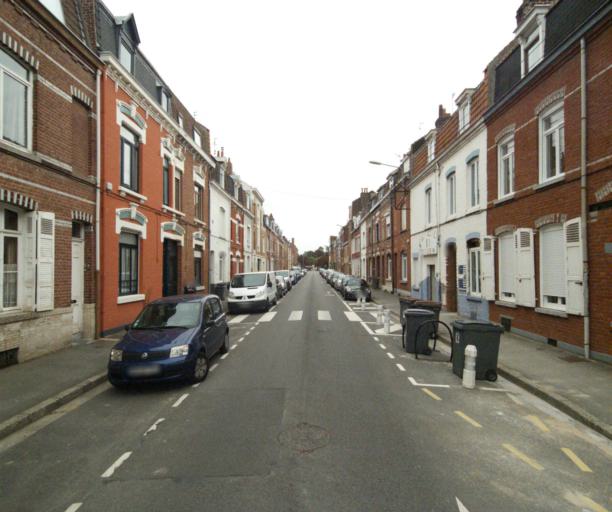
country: FR
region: Nord-Pas-de-Calais
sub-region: Departement du Nord
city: Lambersart
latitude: 50.6434
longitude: 3.0241
